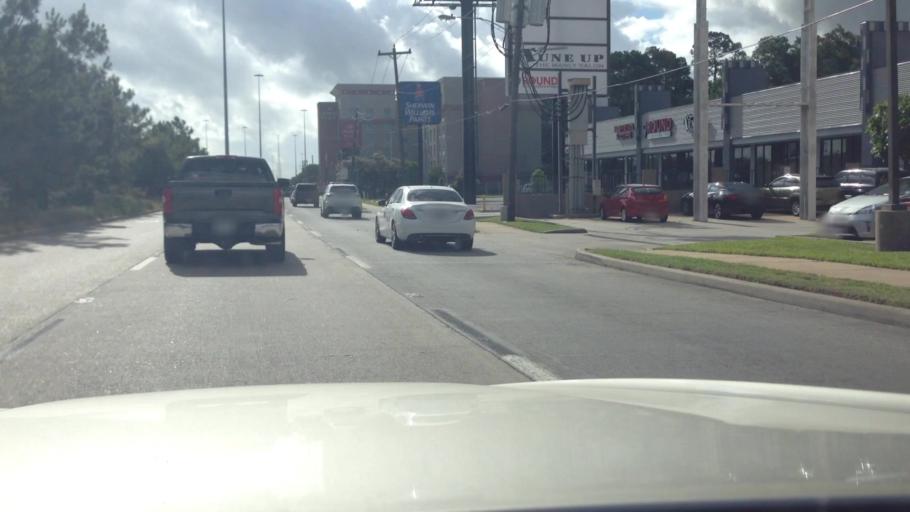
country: US
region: Texas
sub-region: Harris County
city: Hunters Creek Village
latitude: 29.7837
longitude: -95.4671
